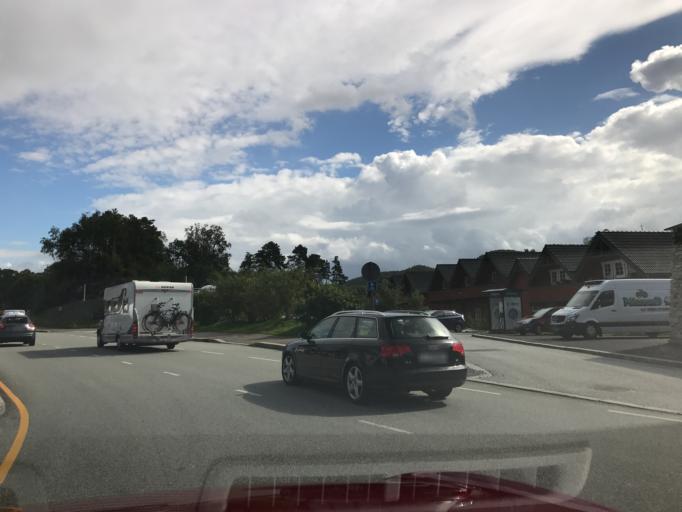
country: NO
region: Hordaland
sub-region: Os
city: Hagavik
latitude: 60.1458
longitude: 5.4271
